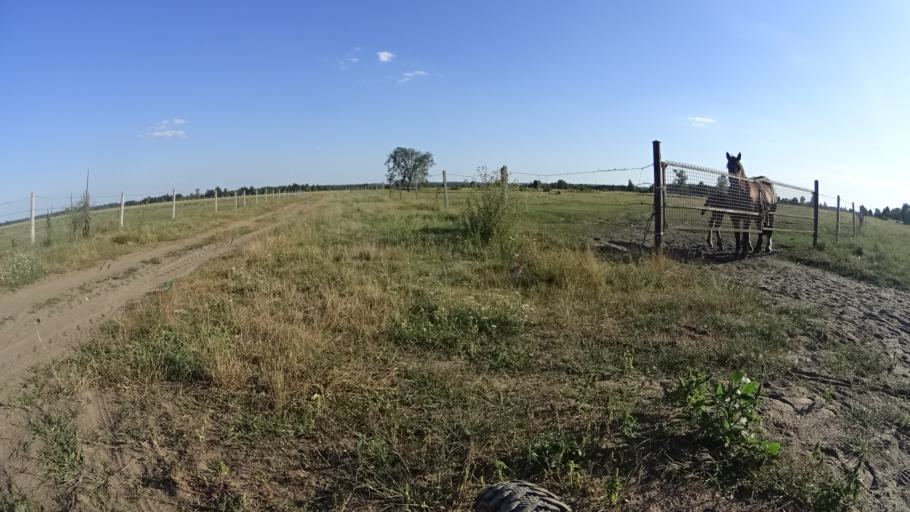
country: PL
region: Masovian Voivodeship
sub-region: Powiat bialobrzeski
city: Wysmierzyce
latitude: 51.6608
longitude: 20.8663
